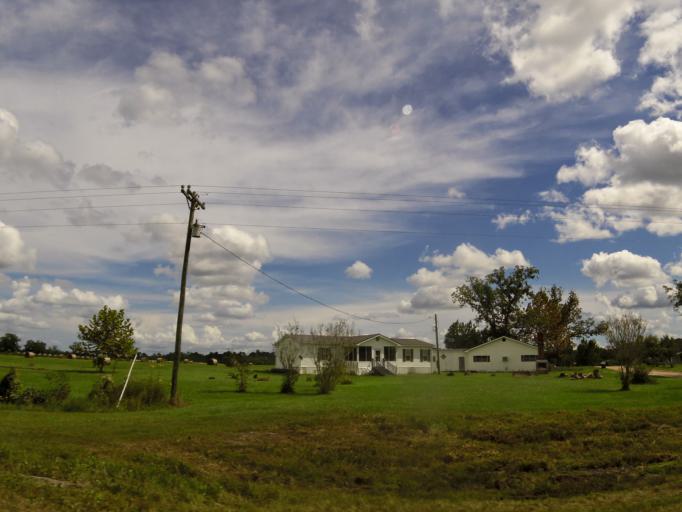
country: US
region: Georgia
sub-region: Brantley County
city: Nahunta
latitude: 31.1210
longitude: -82.0019
